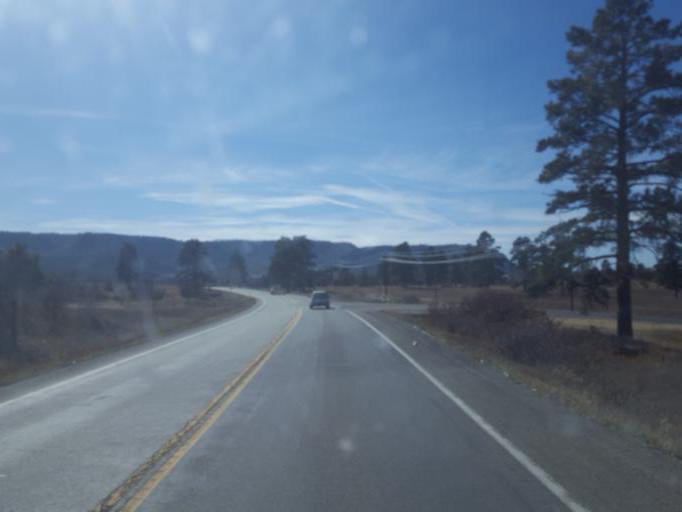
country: US
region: Colorado
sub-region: Archuleta County
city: Pagosa Springs
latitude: 37.2424
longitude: -107.0984
